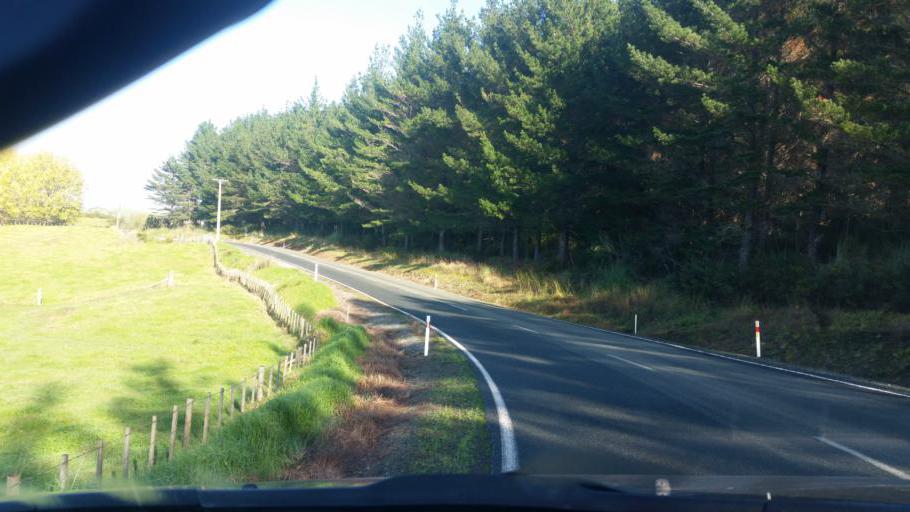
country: NZ
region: Auckland
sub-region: Auckland
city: Wellsford
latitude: -36.2280
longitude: 174.4472
